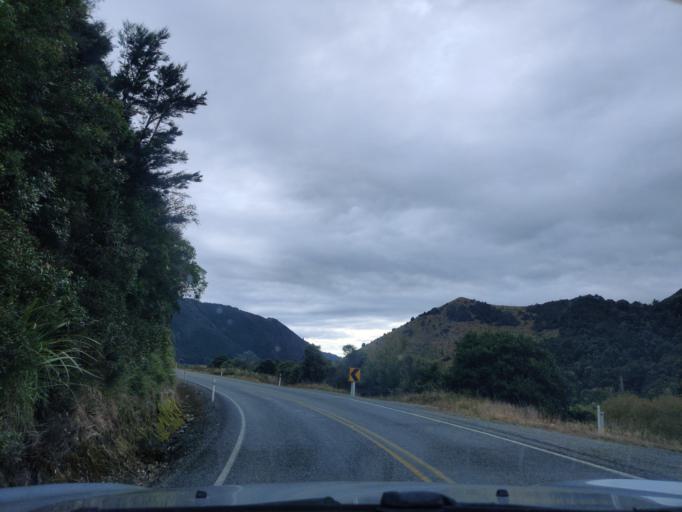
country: NZ
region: Tasman
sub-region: Tasman District
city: Wakefield
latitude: -41.6990
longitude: 172.6237
